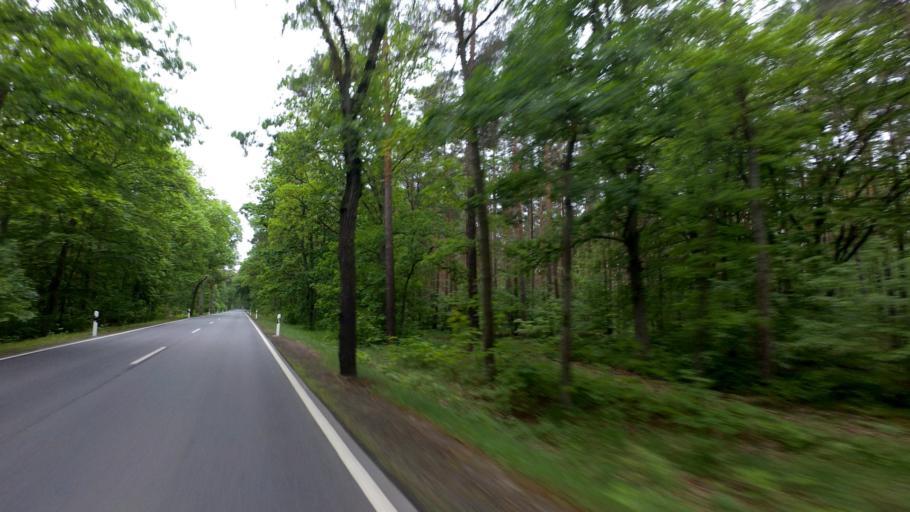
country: DE
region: Brandenburg
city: Marienwerder
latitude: 52.8407
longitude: 13.5132
